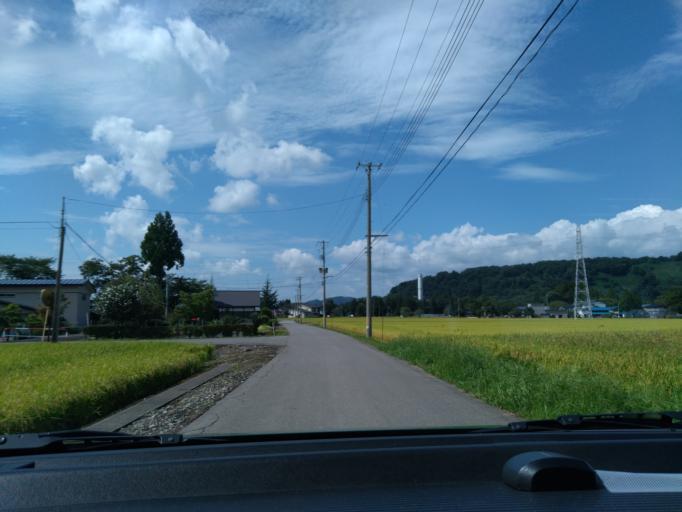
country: JP
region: Akita
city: Kakunodatemachi
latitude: 39.5782
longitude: 140.5880
